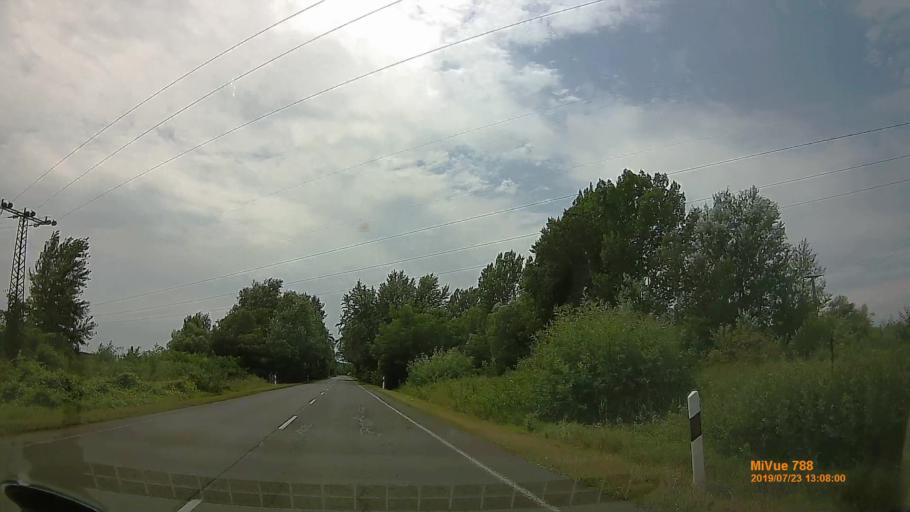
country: HU
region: Szabolcs-Szatmar-Bereg
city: Tiszavasvari
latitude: 47.9502
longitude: 21.3285
